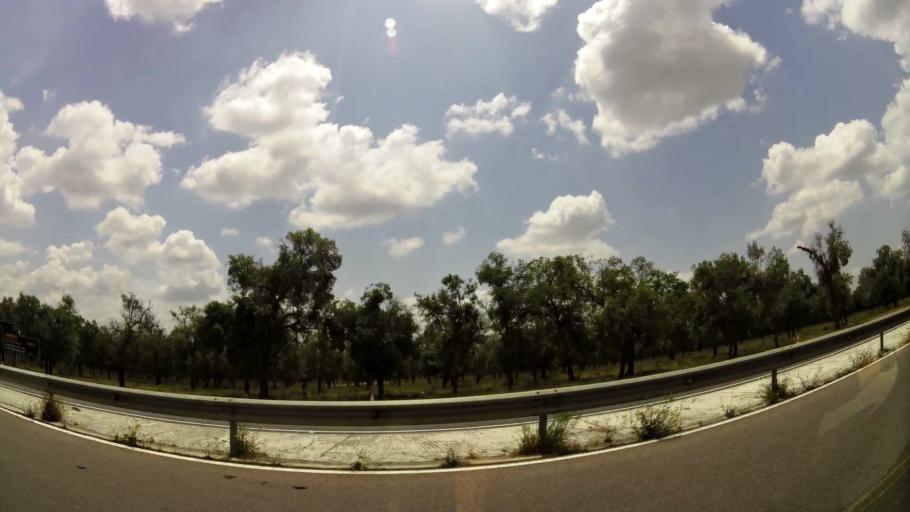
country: MA
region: Rabat-Sale-Zemmour-Zaer
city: Sale
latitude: 34.0193
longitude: -6.5694
